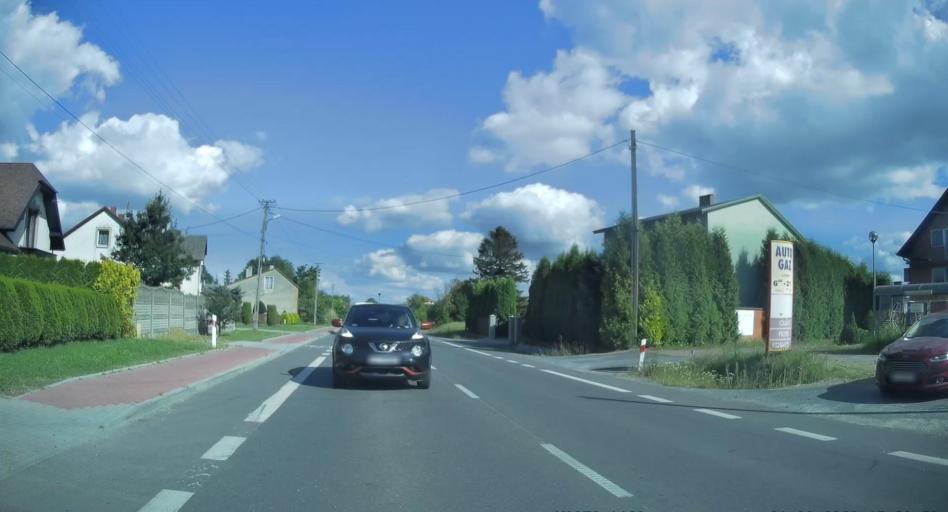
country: PL
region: Swietokrzyskie
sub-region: Powiat kielecki
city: Bodzentyn
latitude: 50.9335
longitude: 20.9675
